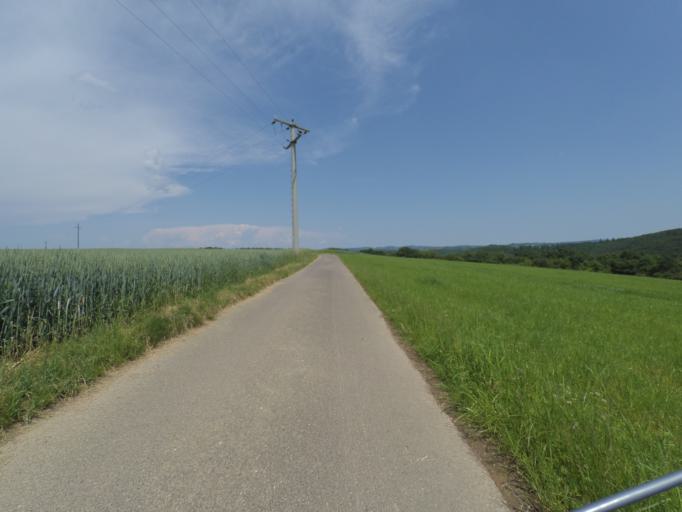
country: DE
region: Rheinland-Pfalz
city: Beulich
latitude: 50.1795
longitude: 7.4560
